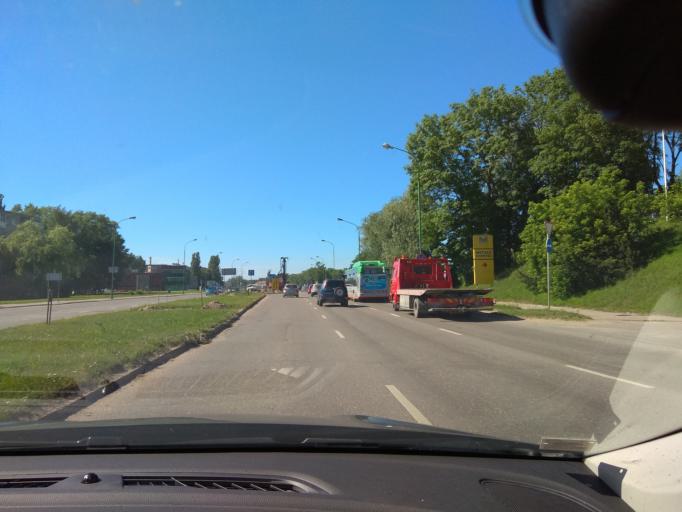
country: LT
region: Klaipedos apskritis
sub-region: Klaipeda
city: Klaipeda
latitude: 55.7001
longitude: 21.1675
